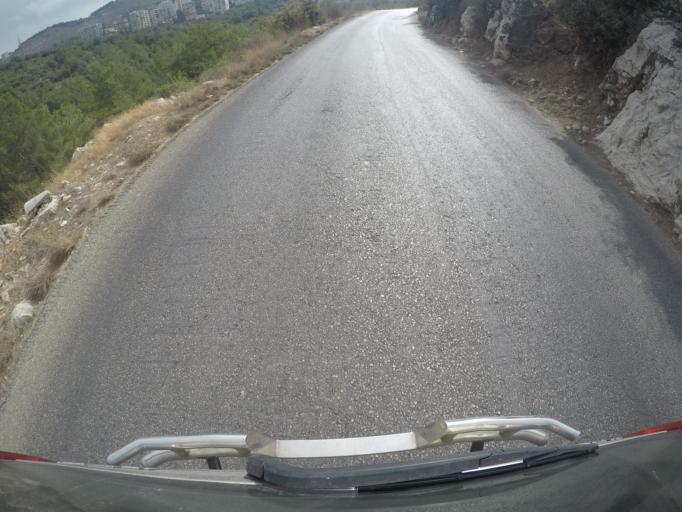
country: LB
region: Mont-Liban
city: Beit ed Dine
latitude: 33.7371
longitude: 35.4830
